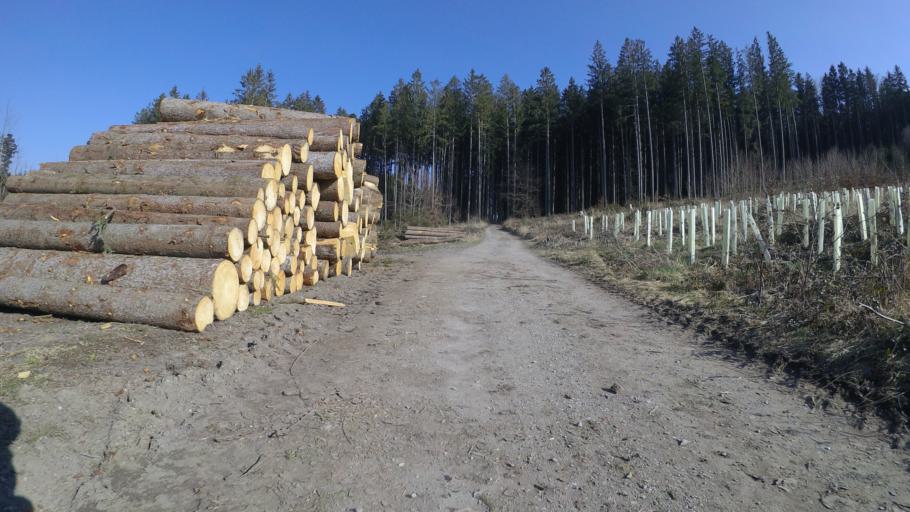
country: DE
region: Bavaria
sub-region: Upper Bavaria
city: Chieming
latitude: 47.8806
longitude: 12.5675
